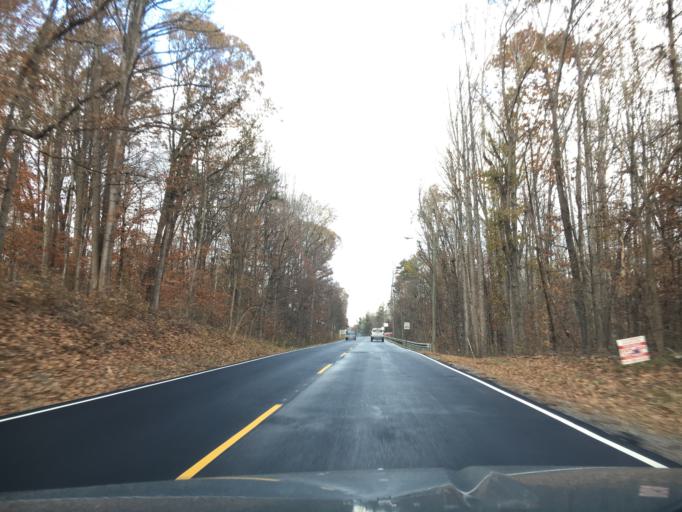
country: US
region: Virginia
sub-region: Prince Edward County
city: Farmville
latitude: 37.3150
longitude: -78.3861
